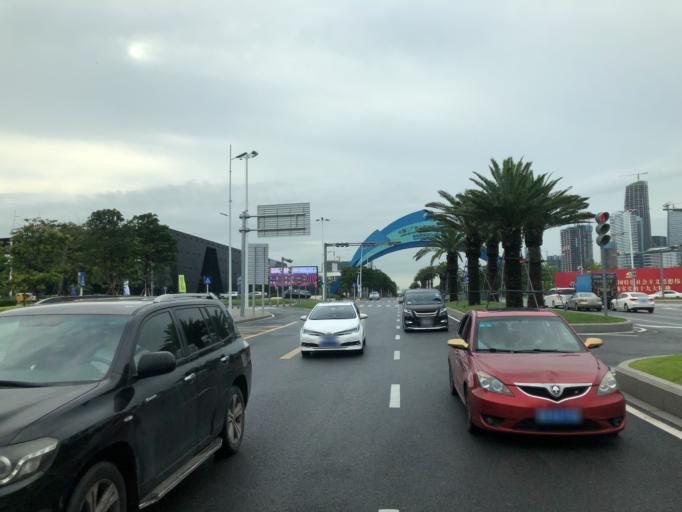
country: CN
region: Guangdong
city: Nantou
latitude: 22.5201
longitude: 113.8996
